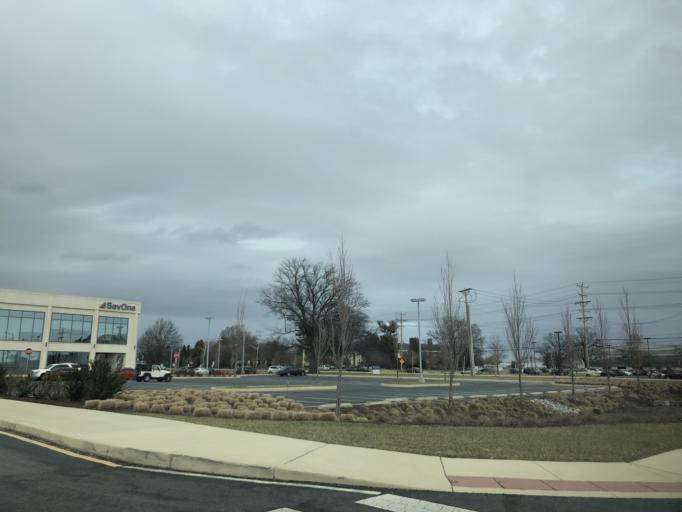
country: US
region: Delaware
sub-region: New Castle County
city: Newark
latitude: 39.6632
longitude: -75.7533
